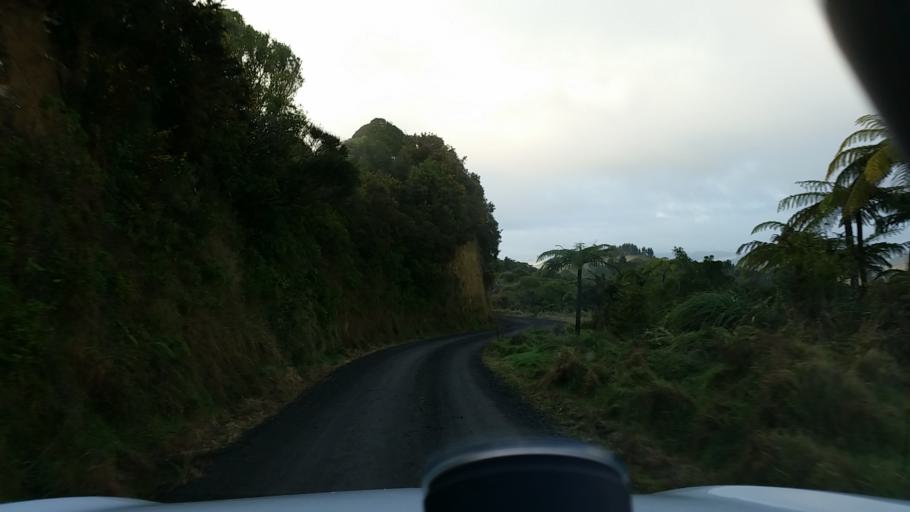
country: NZ
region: Taranaki
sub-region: South Taranaki District
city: Eltham
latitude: -39.4474
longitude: 174.4543
